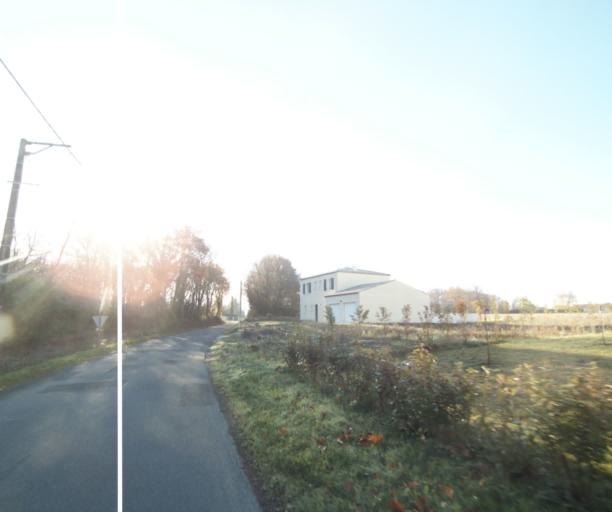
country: FR
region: Poitou-Charentes
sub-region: Departement de la Charente-Maritime
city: Fontcouverte
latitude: 45.7623
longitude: -0.5852
